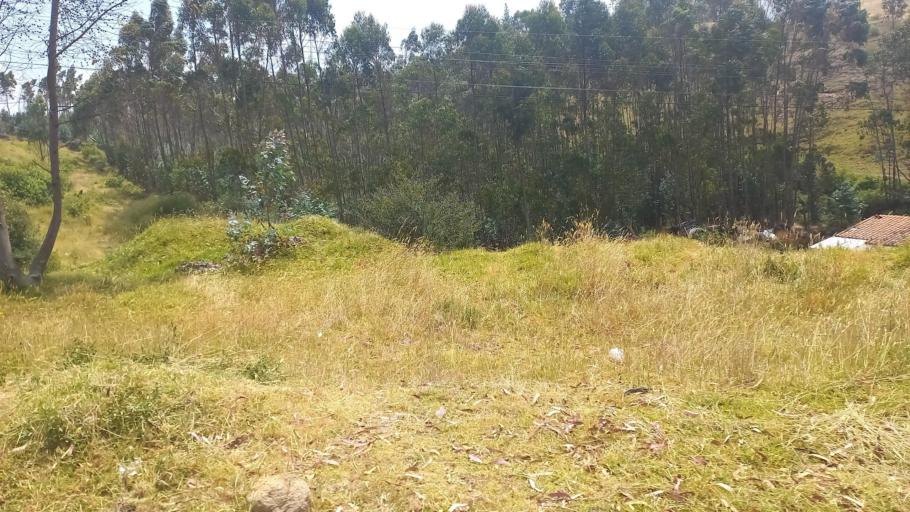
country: EC
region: Pichincha
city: Cayambe
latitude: 0.1749
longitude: -78.0901
